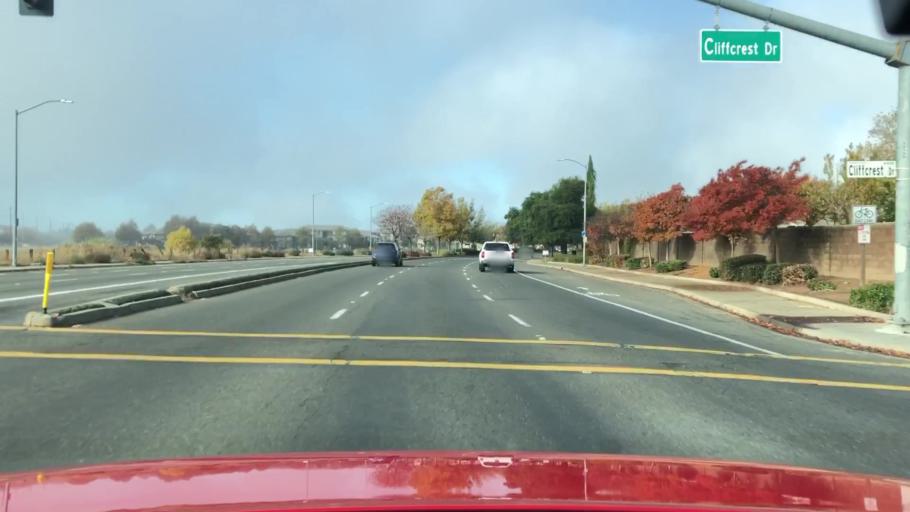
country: US
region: California
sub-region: Sacramento County
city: Laguna
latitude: 38.4530
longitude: -121.3959
